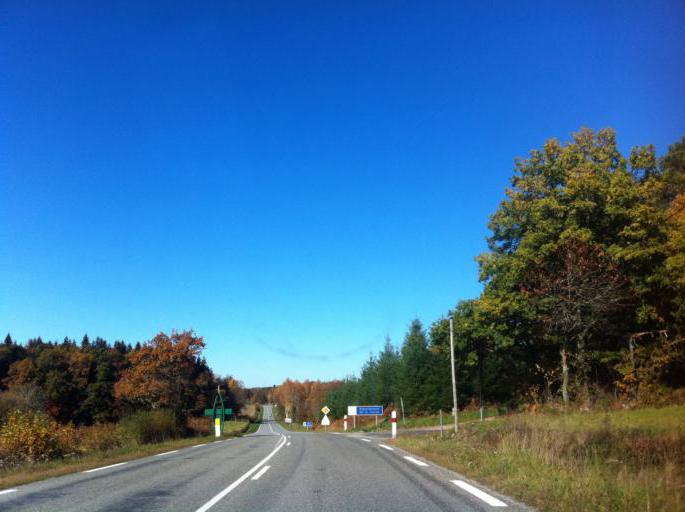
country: FR
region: Auvergne
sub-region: Departement du Puy-de-Dome
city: Gelles
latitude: 45.8607
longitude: 2.6072
